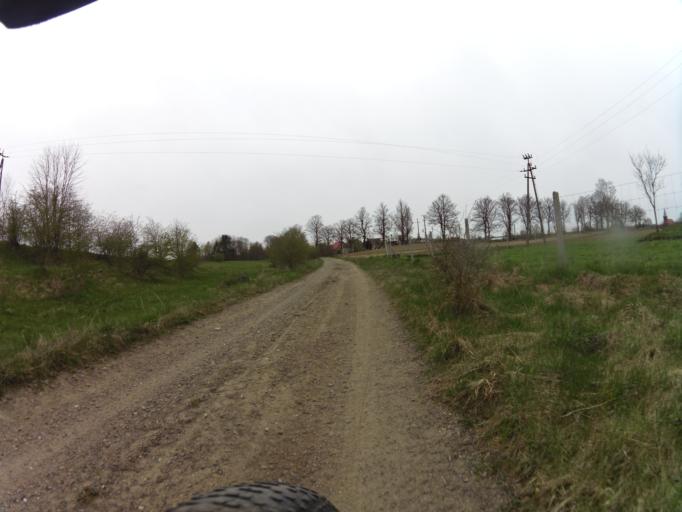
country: PL
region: West Pomeranian Voivodeship
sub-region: Powiat koszalinski
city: Bobolice
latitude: 53.9912
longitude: 16.6821
